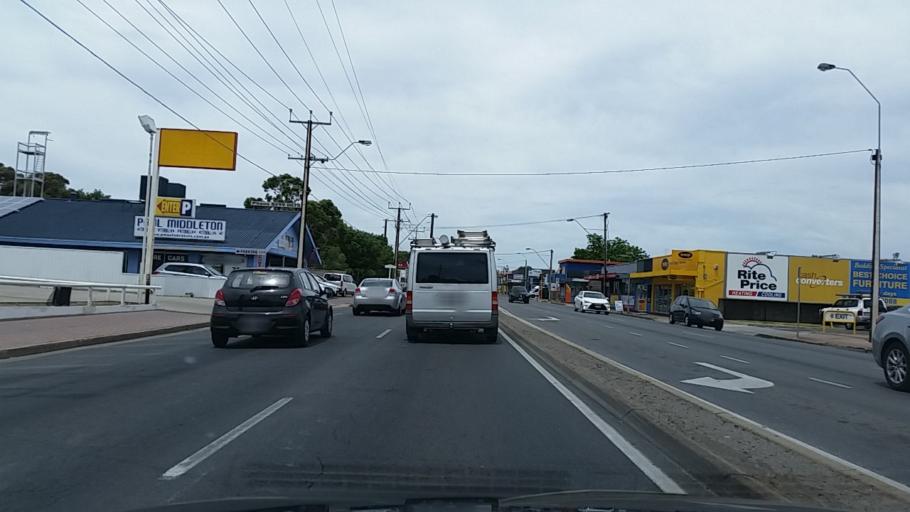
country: AU
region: South Australia
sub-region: Marion
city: Clovelly Park
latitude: -34.9930
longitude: 138.5749
